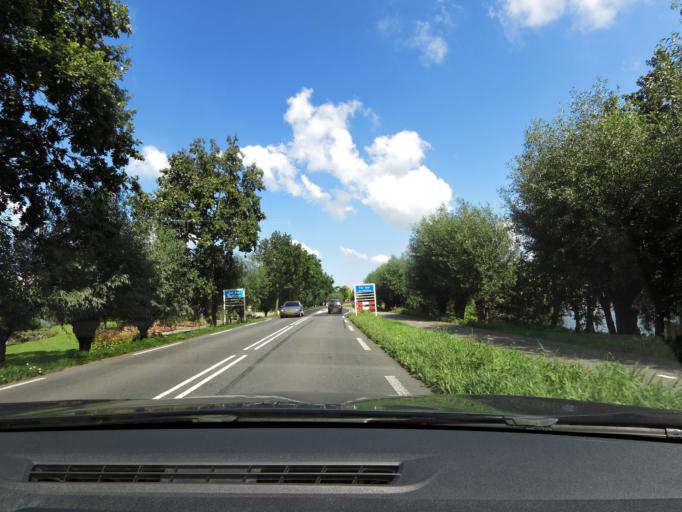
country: NL
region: South Holland
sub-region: Gemeente Alphen aan den Rijn
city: Alphen aan den Rijn
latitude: 52.1617
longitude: 4.7088
